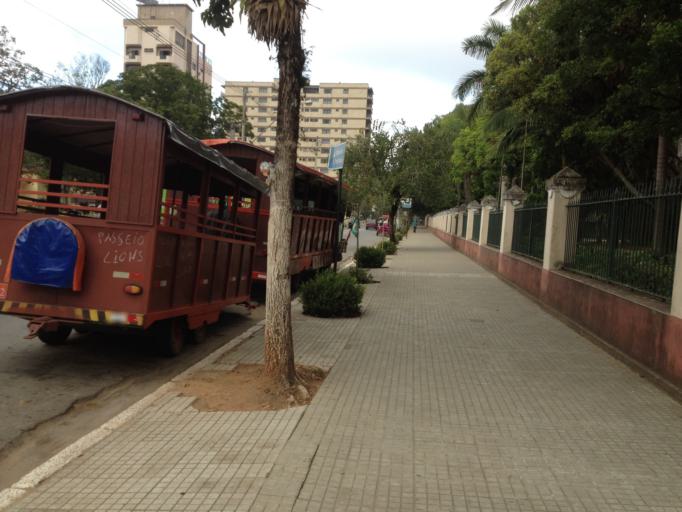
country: BR
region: Minas Gerais
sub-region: Caxambu
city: Caxambu
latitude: -21.9810
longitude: -44.9350
